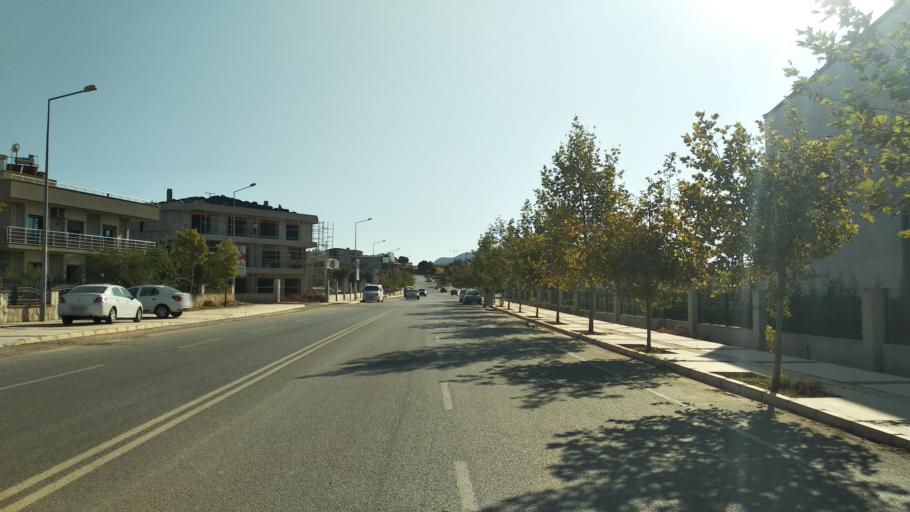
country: TR
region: Izmir
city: Urla
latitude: 38.3567
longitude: 26.8727
